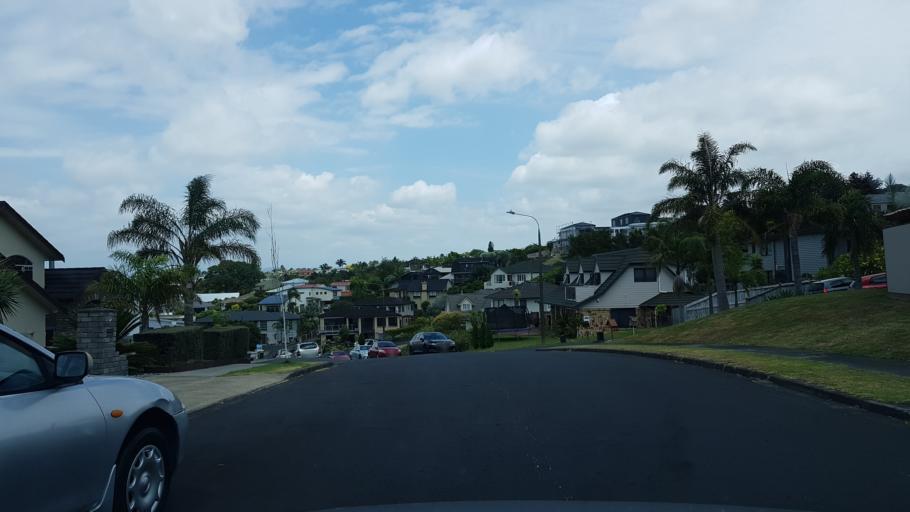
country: NZ
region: Auckland
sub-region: Auckland
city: Rosebank
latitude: -36.8007
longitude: 174.6491
